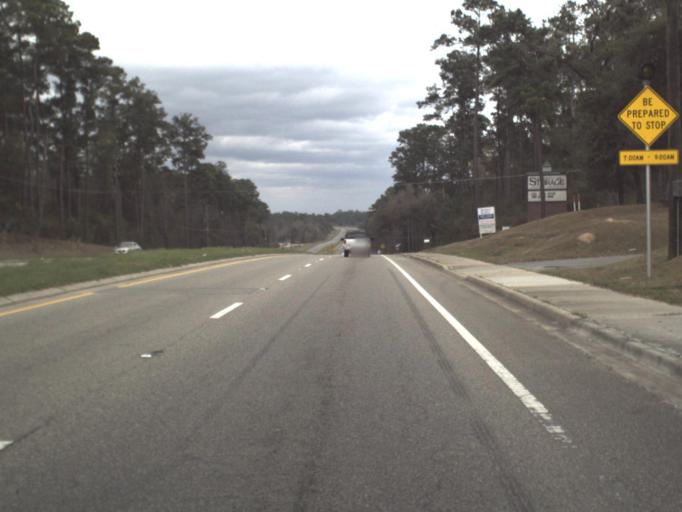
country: US
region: Florida
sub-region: Leon County
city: Tallahassee
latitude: 30.5660
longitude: -84.2125
